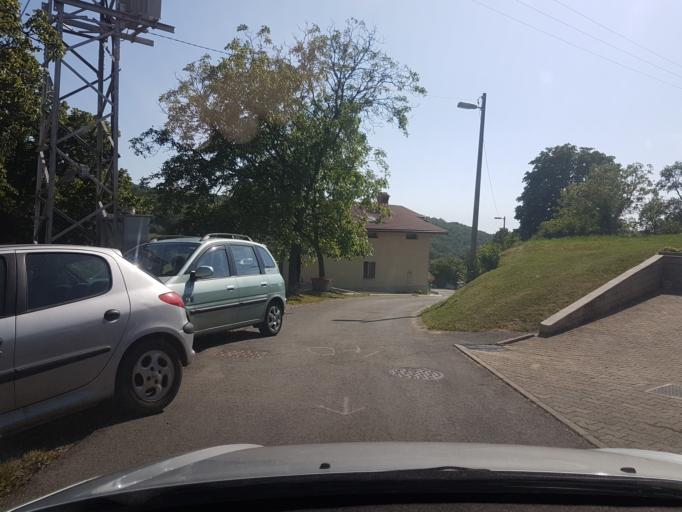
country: SI
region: Vipava
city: Vipava
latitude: 45.7678
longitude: 13.9757
